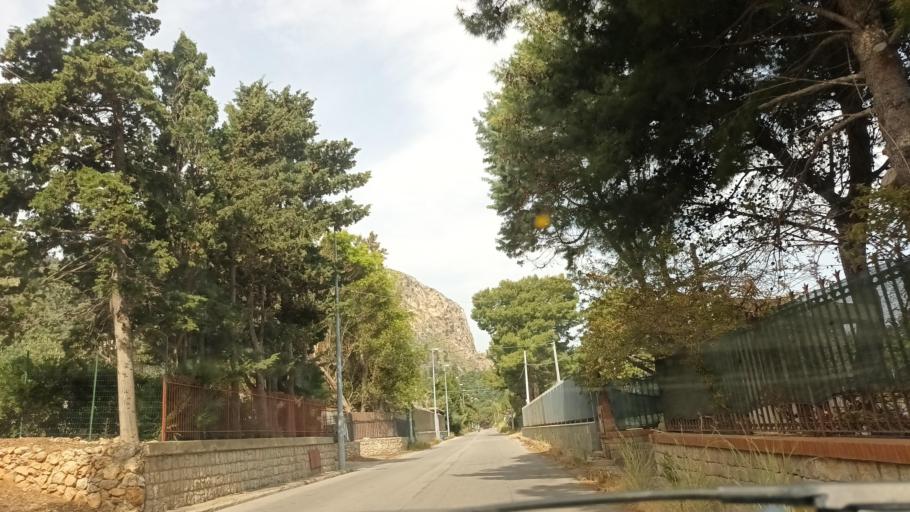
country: IT
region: Sicily
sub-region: Palermo
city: Santa Flavia
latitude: 38.1124
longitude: 13.5243
